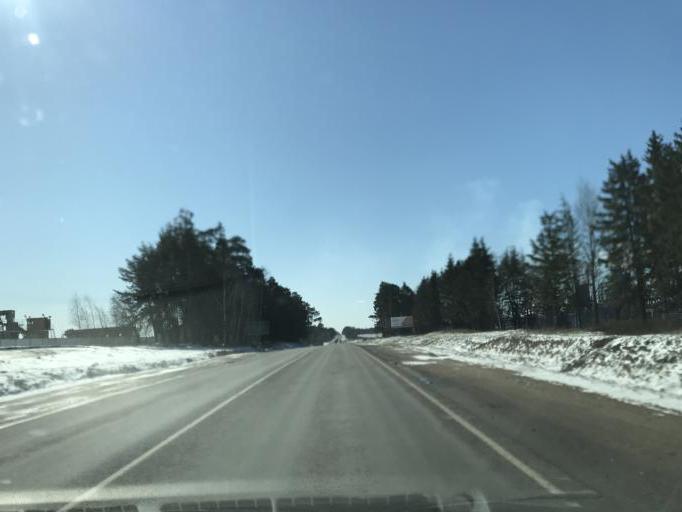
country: BY
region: Mogilev
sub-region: Mahilyowski Rayon
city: Veyno
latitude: 53.8299
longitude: 30.3604
